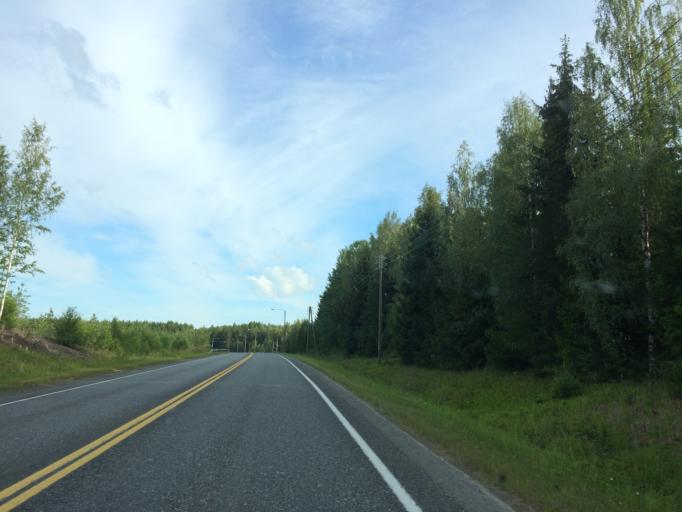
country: FI
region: Haeme
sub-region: Haemeenlinna
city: Janakkala
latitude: 60.9117
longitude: 24.5517
